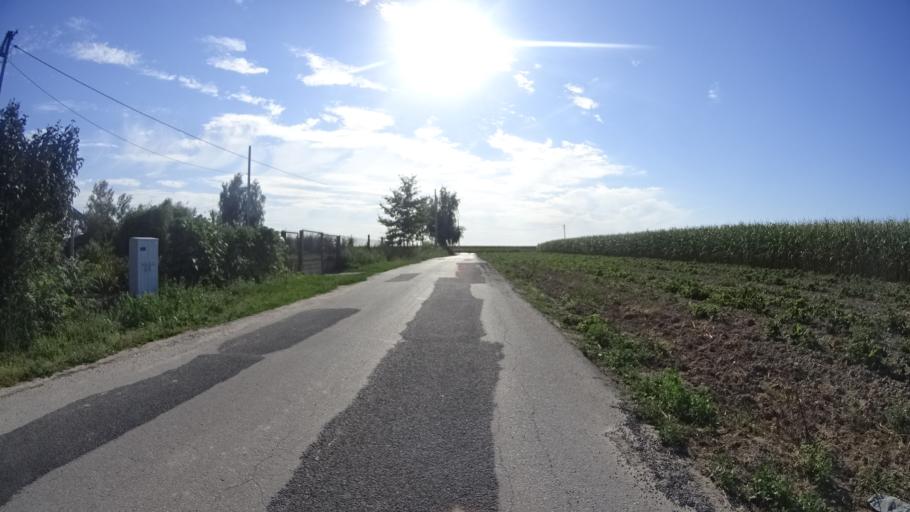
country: PL
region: Masovian Voivodeship
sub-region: Powiat bialobrzeski
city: Wysmierzyce
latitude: 51.6696
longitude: 20.8070
